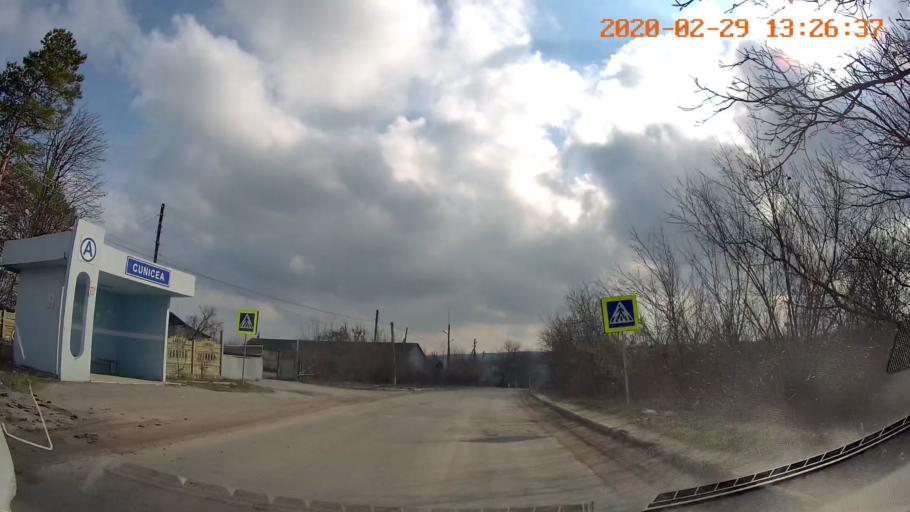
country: MD
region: Telenesti
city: Camenca
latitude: 47.9187
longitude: 28.6384
